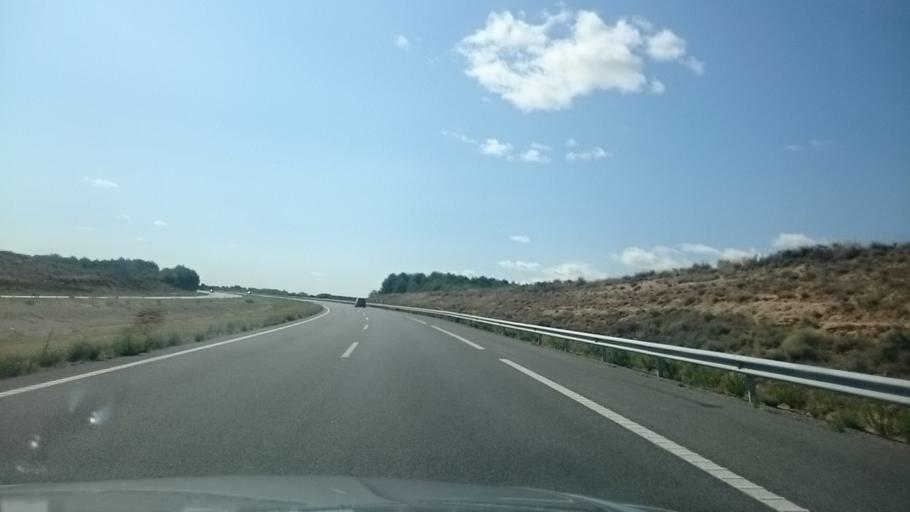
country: ES
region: Navarre
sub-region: Provincia de Navarra
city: Murchante
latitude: 42.0552
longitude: -1.6870
